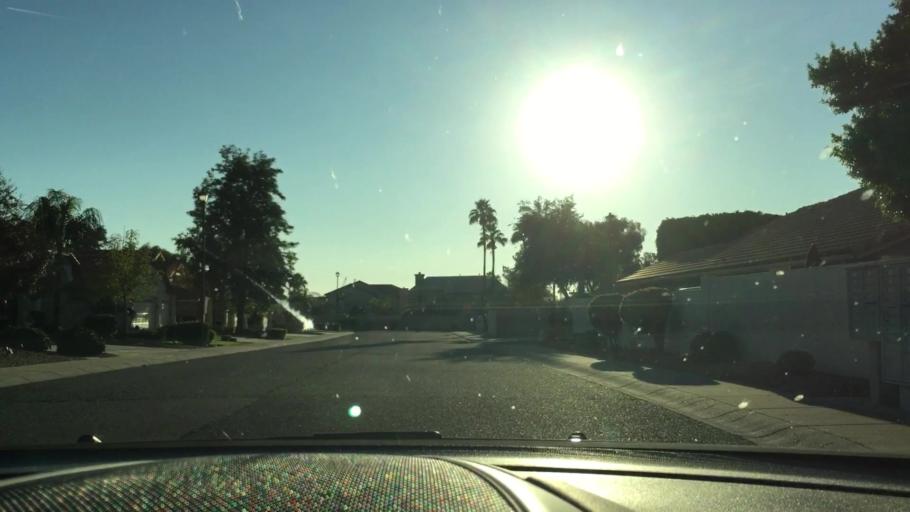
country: US
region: Arizona
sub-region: Maricopa County
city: Sun City
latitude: 33.6613
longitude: -112.2276
